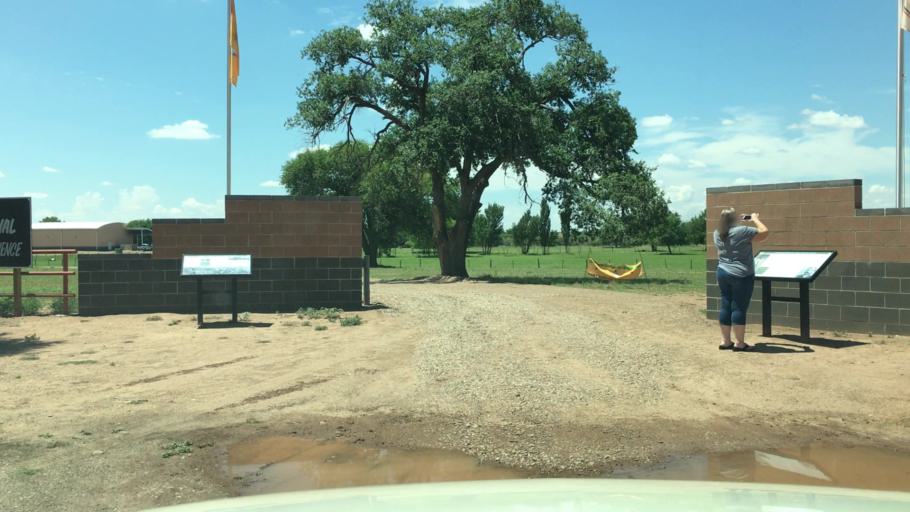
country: US
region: New Mexico
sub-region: De Baca County
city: Fort Sumner
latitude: 34.4044
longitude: -104.1938
